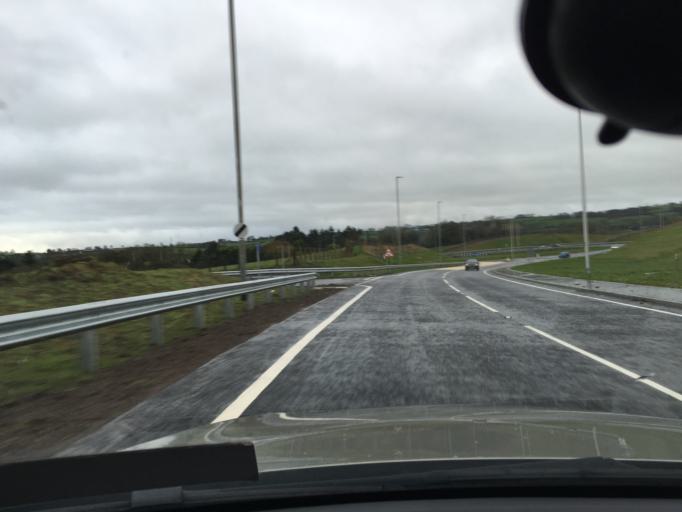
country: GB
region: Northern Ireland
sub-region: Larne District
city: Larne
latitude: 54.8340
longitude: -5.8753
